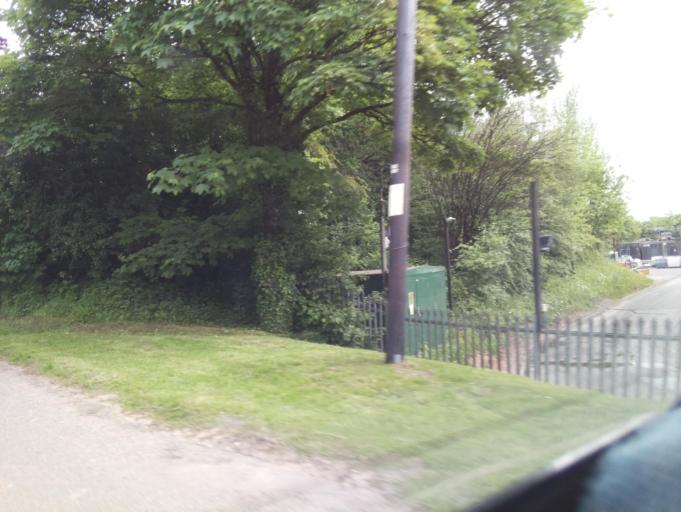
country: GB
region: England
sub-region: Herefordshire
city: Ledbury
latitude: 52.0506
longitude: -2.4312
